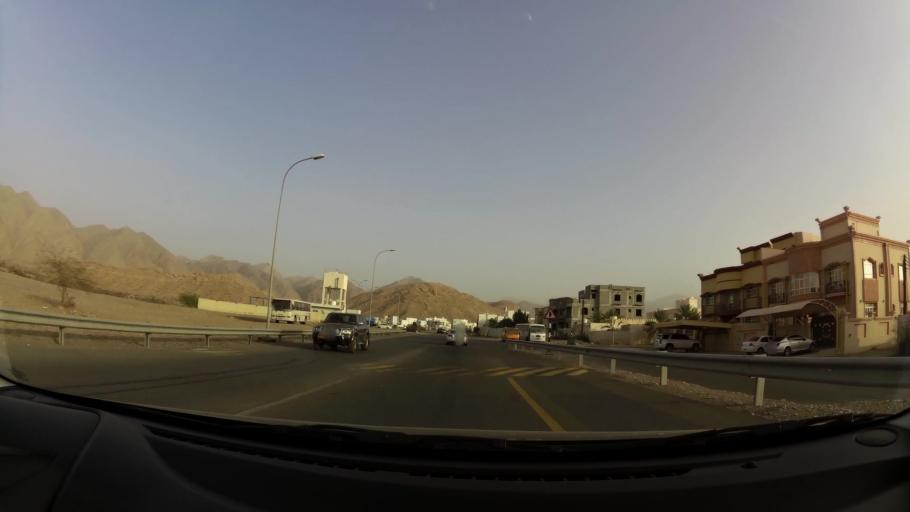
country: OM
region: Muhafazat Masqat
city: Bawshar
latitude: 23.5138
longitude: 58.3457
